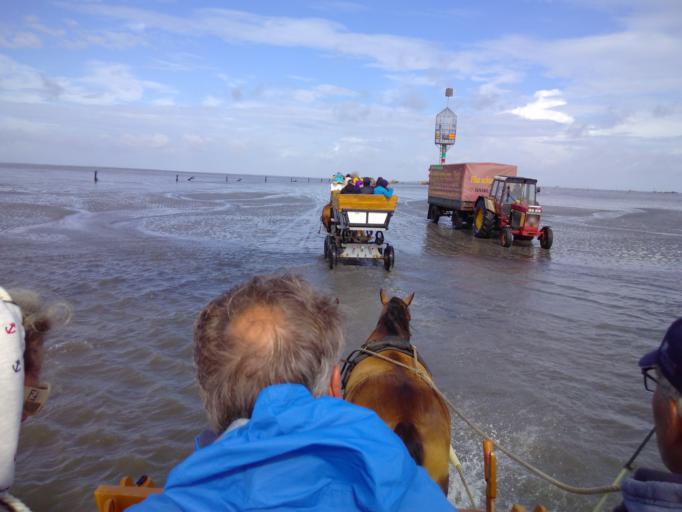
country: DE
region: Lower Saxony
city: Nordholz
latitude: 53.8826
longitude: 8.5752
